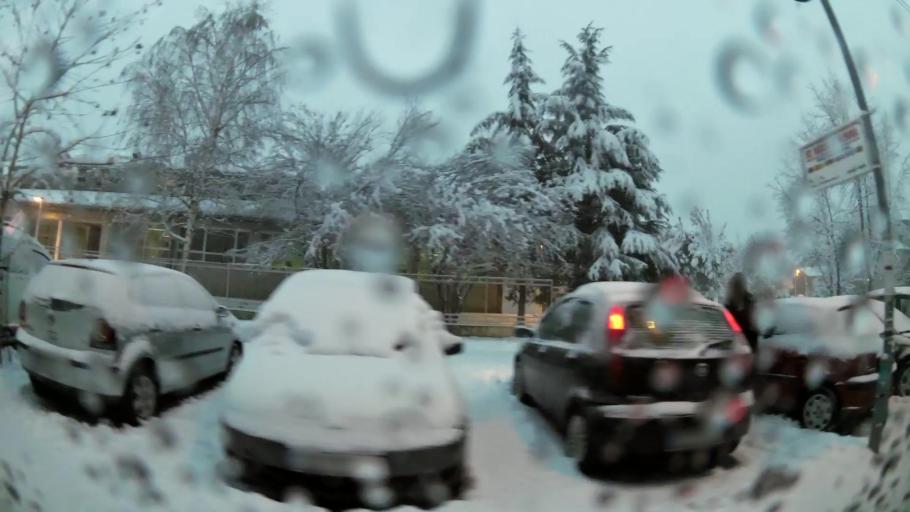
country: RS
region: Central Serbia
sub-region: Belgrade
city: Zemun
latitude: 44.8164
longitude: 20.3869
